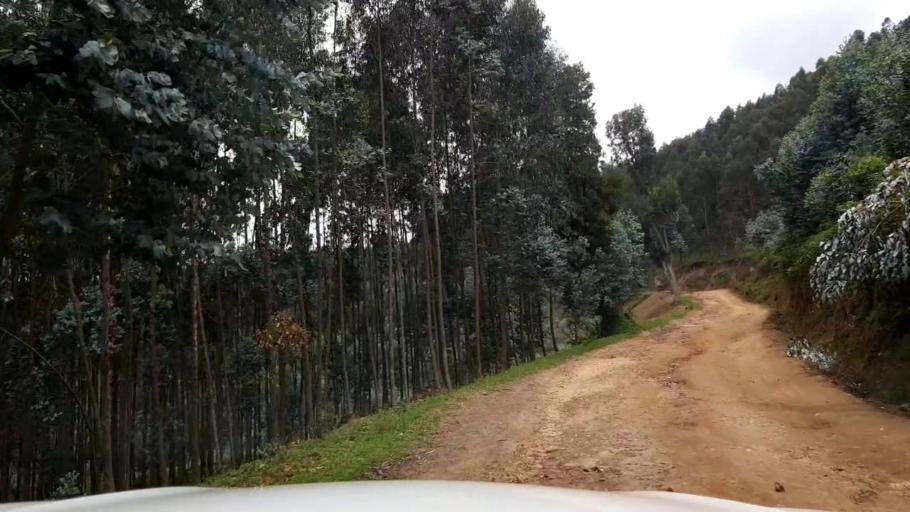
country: RW
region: Western Province
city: Kibuye
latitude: -1.9599
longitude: 29.3959
